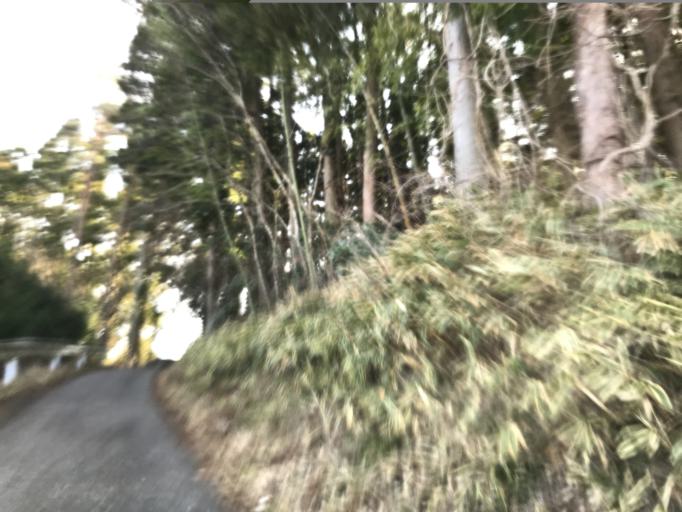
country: JP
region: Fukushima
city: Iwaki
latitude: 37.0503
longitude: 140.7921
